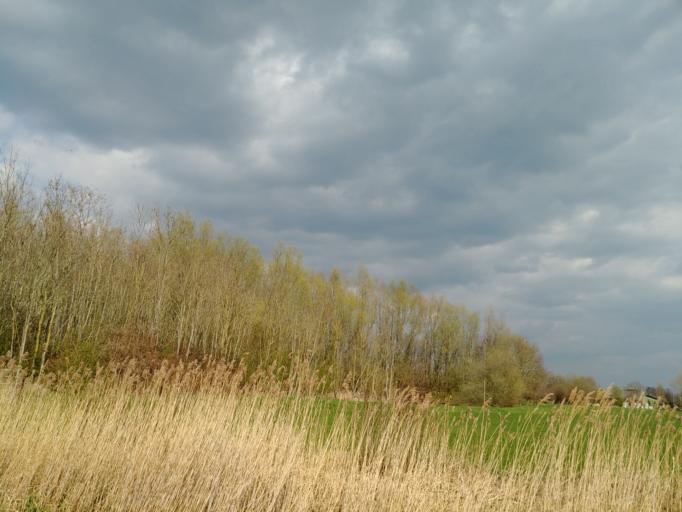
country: NL
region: Gelderland
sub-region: Gemeente Voorst
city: Twello
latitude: 52.2630
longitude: 6.0658
